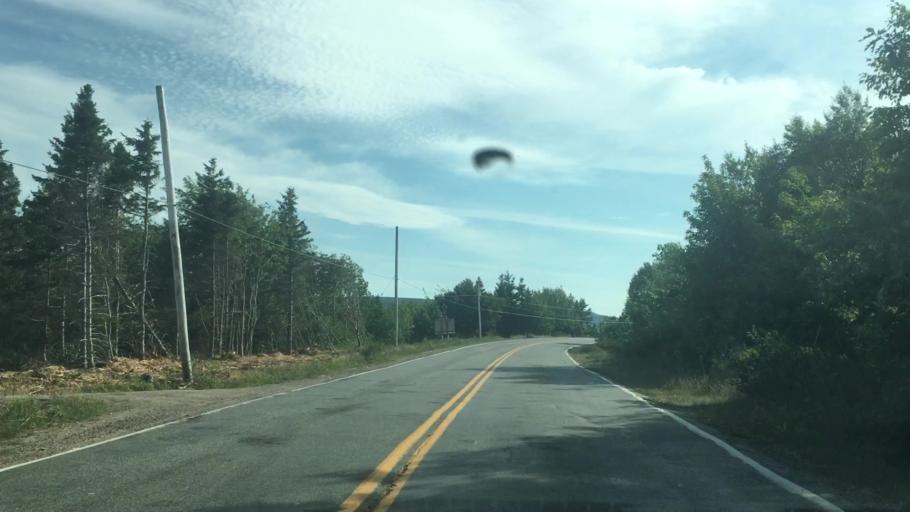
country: CA
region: Nova Scotia
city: Sydney Mines
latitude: 46.8793
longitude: -60.5166
